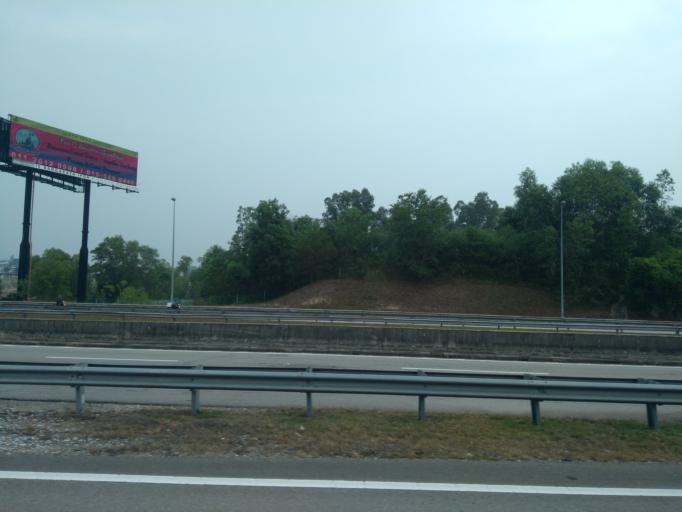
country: MY
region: Perak
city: Ipoh
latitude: 4.6667
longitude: 101.0759
